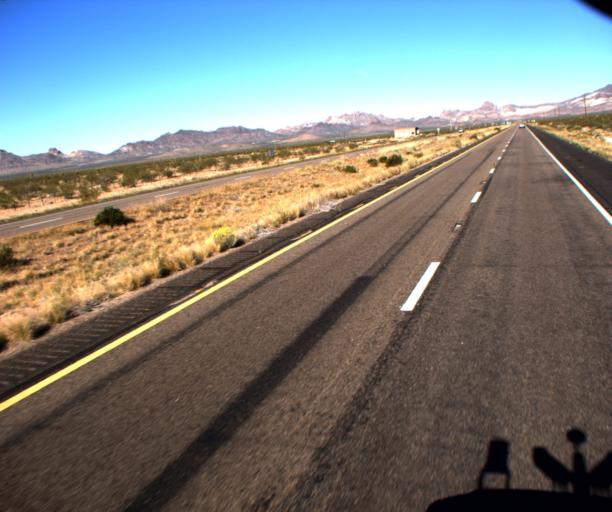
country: US
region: Arizona
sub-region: Mohave County
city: Golden Valley
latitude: 35.2262
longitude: -114.3002
